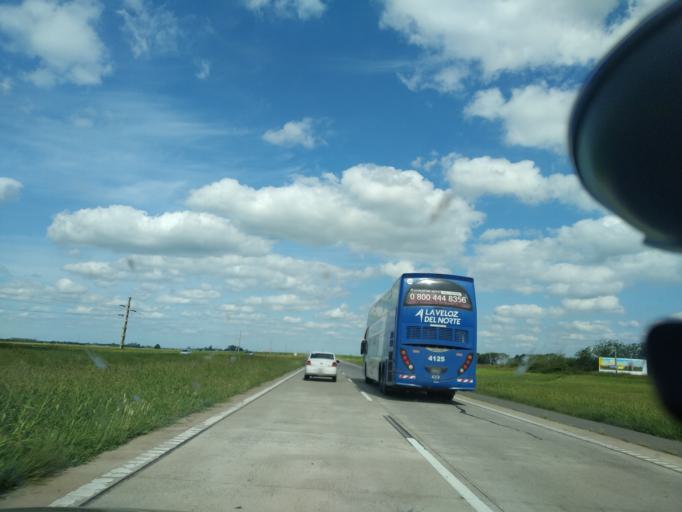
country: AR
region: Santa Fe
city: Canada de Gomez
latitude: -32.8623
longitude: -61.2997
